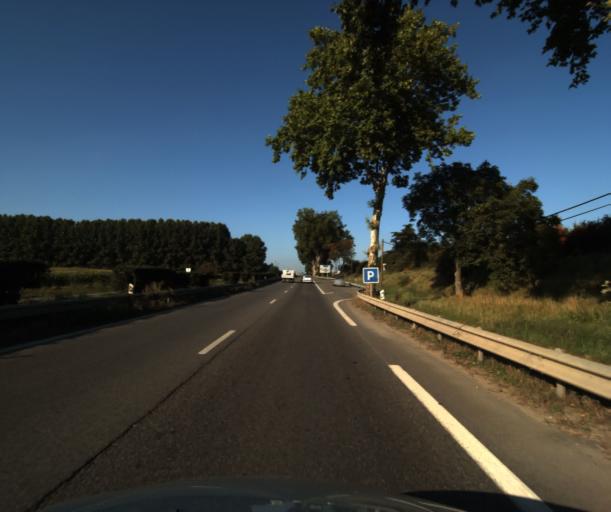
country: FR
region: Midi-Pyrenees
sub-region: Departement de la Haute-Garonne
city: Roquettes
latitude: 43.5036
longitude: 1.3585
